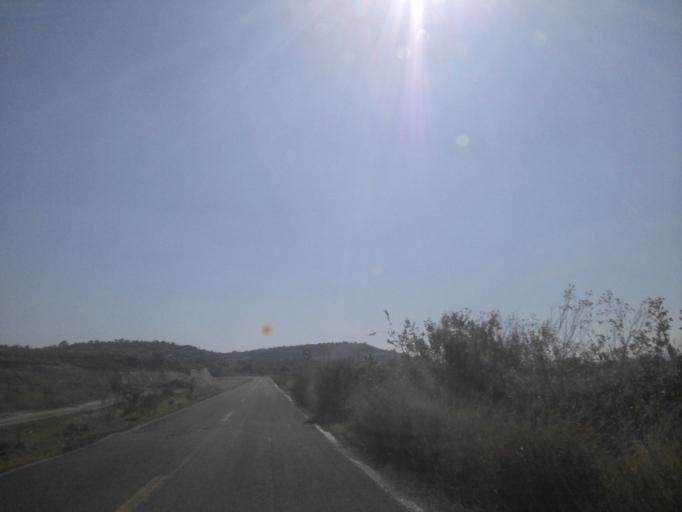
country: MX
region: Jalisco
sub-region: Arandas
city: Santiaguito (Santiaguito de Velazquez)
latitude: 20.7886
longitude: -102.2707
